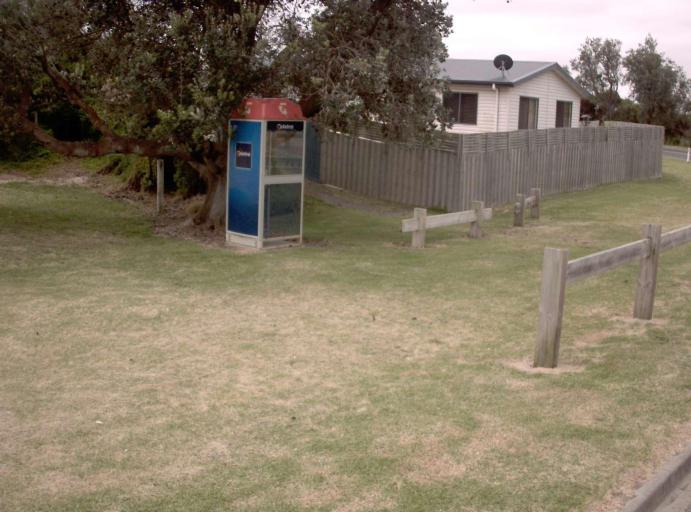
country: AU
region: Victoria
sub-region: Wellington
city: Sale
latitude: -38.5506
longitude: 146.9780
